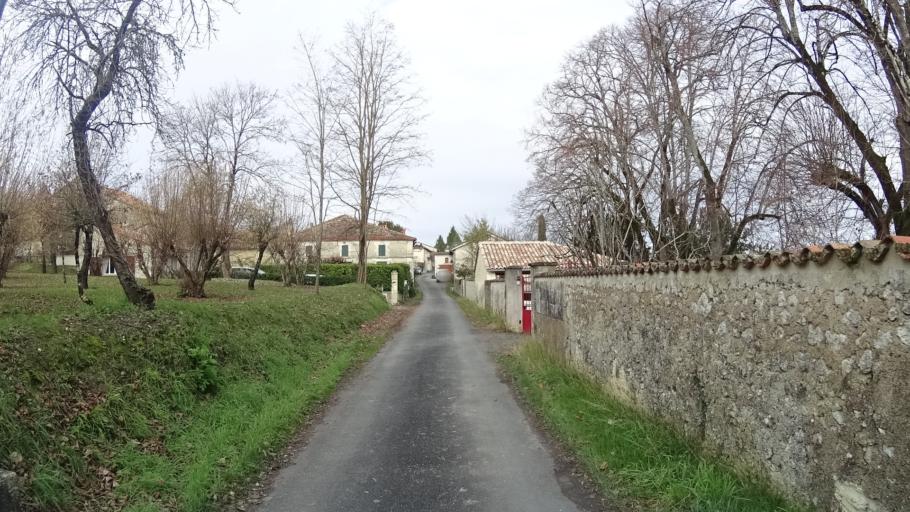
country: FR
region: Aquitaine
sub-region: Departement de la Dordogne
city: Saint-Aulaye
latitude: 45.2414
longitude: 0.1497
